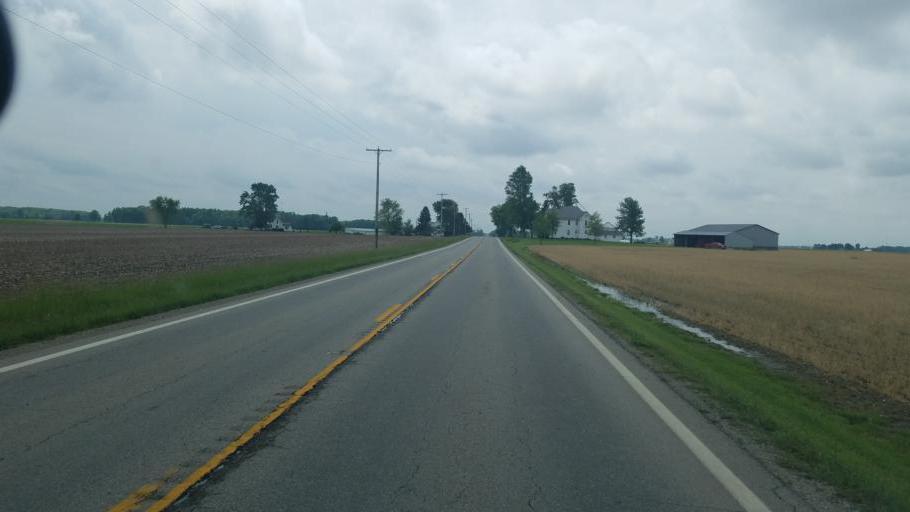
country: US
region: Ohio
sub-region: Marion County
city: Prospect
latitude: 40.4362
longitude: -83.2341
